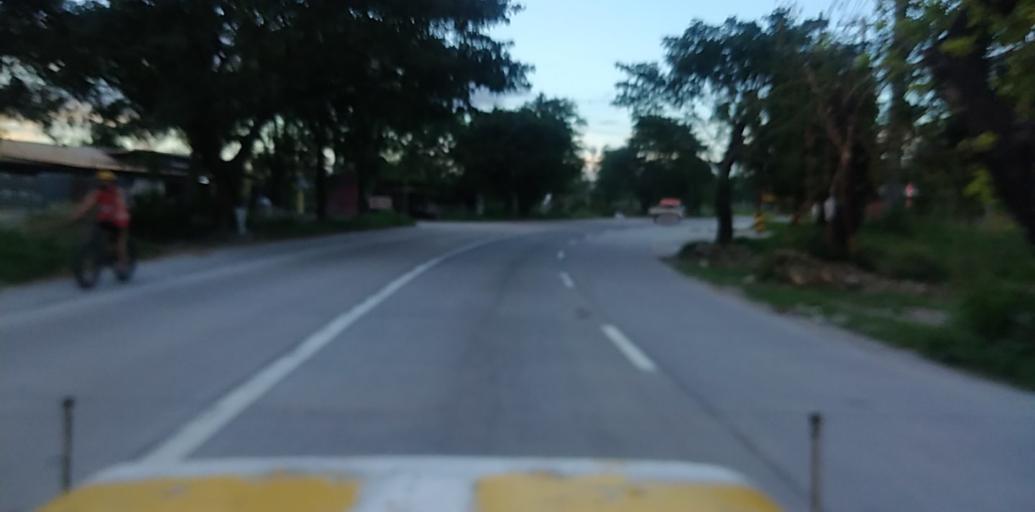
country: PH
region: Central Luzon
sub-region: Province of Pampanga
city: Calibutbut
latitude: 15.1218
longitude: 120.5875
